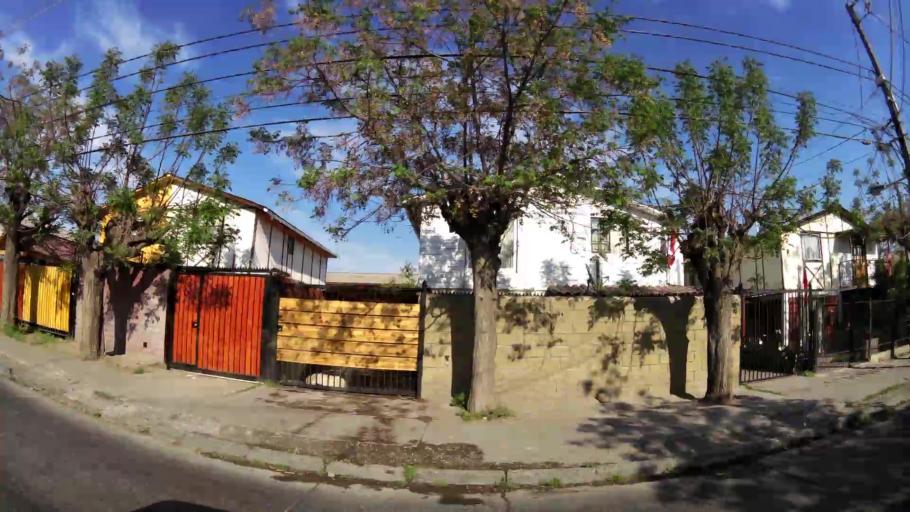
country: CL
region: Santiago Metropolitan
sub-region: Provincia de Santiago
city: La Pintana
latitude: -33.5677
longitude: -70.5926
